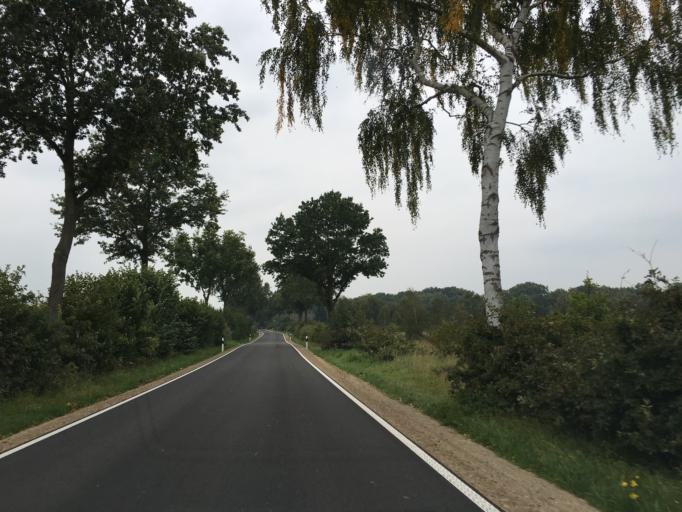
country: DE
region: Schleswig-Holstein
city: Seedorf
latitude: 53.6104
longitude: 10.8877
